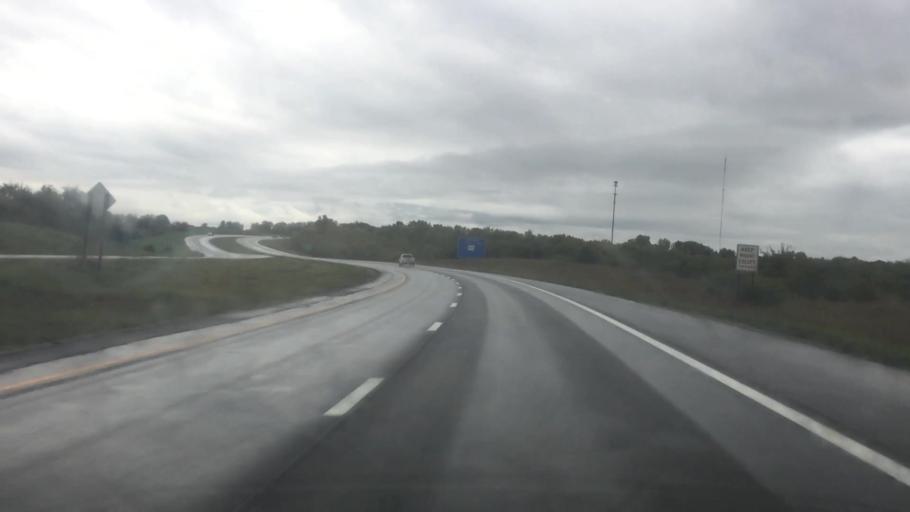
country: US
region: Kansas
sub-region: Johnson County
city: Spring Hill
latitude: 38.7360
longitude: -94.8389
